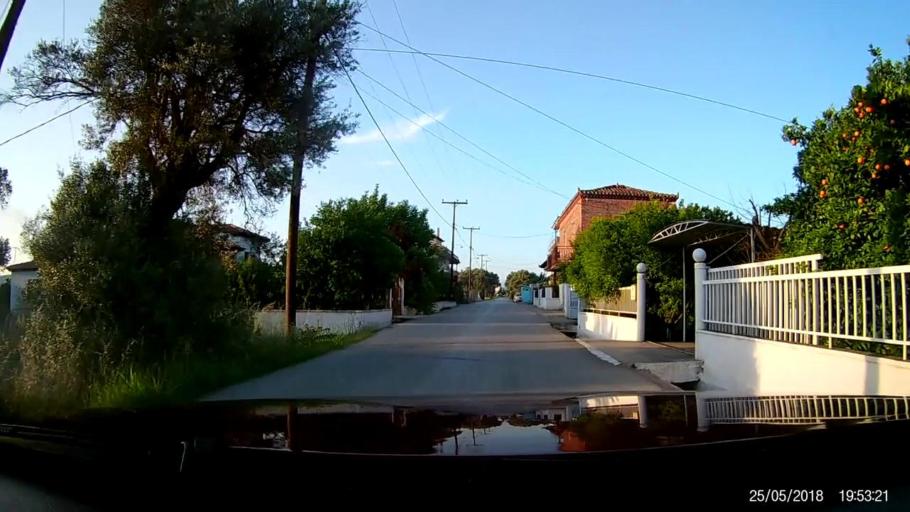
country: GR
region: Central Greece
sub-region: Nomos Evvoias
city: Ayios Nikolaos
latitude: 38.4165
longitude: 23.6503
